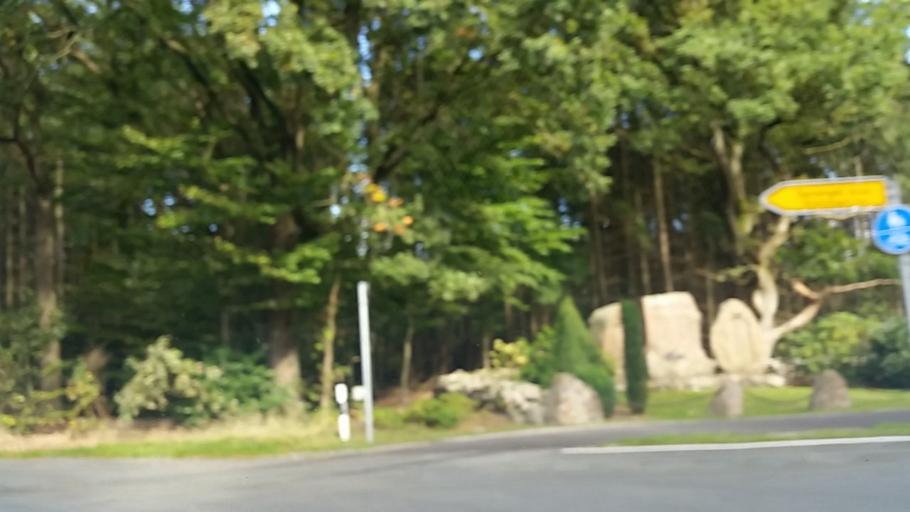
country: DE
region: Lower Saxony
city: Neuenkirchen
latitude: 53.0307
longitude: 9.7353
